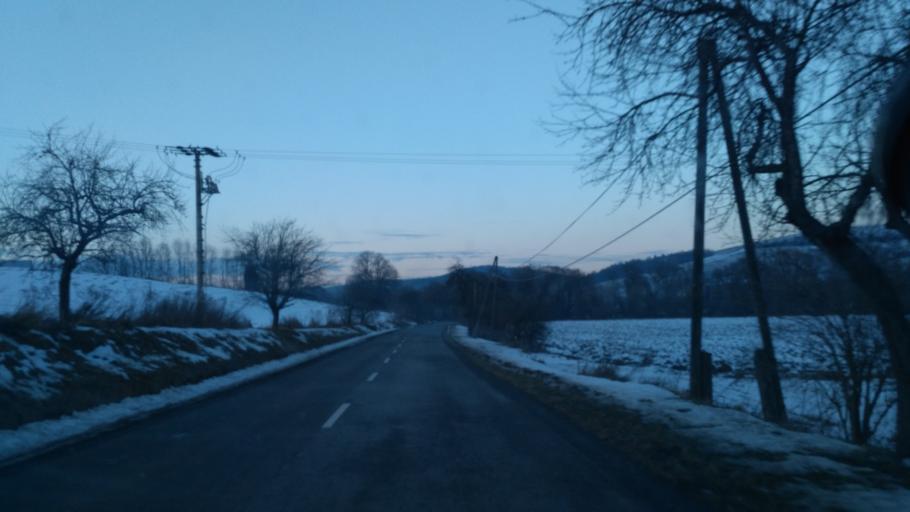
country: SK
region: Presovsky
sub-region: Okres Presov
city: Presov
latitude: 48.9205
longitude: 21.1924
